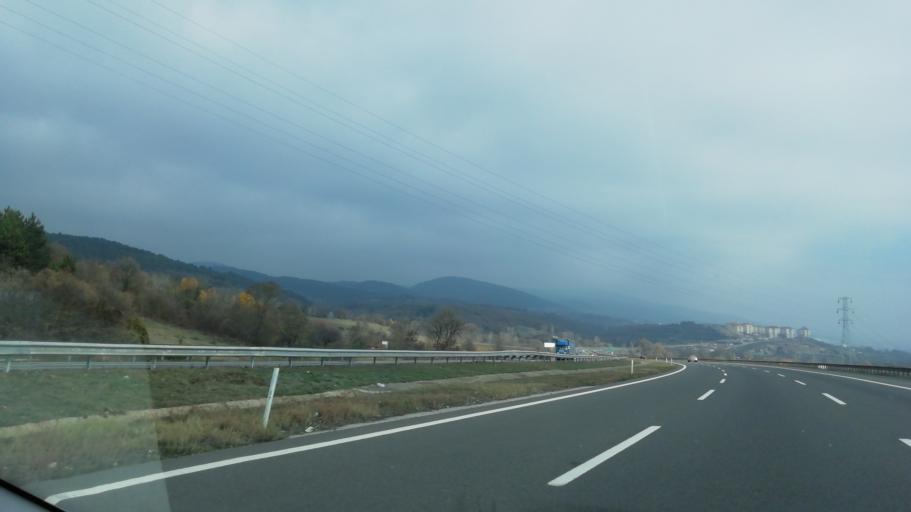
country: TR
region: Bolu
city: Bolu
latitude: 40.7335
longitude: 31.5308
